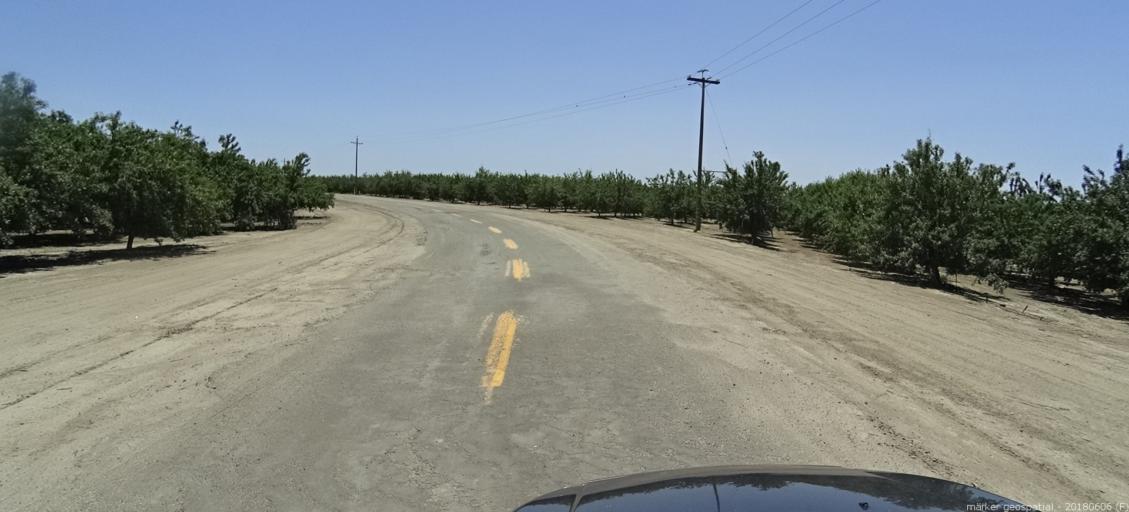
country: US
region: California
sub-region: Fresno County
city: Mendota
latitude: 36.8036
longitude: -120.3402
